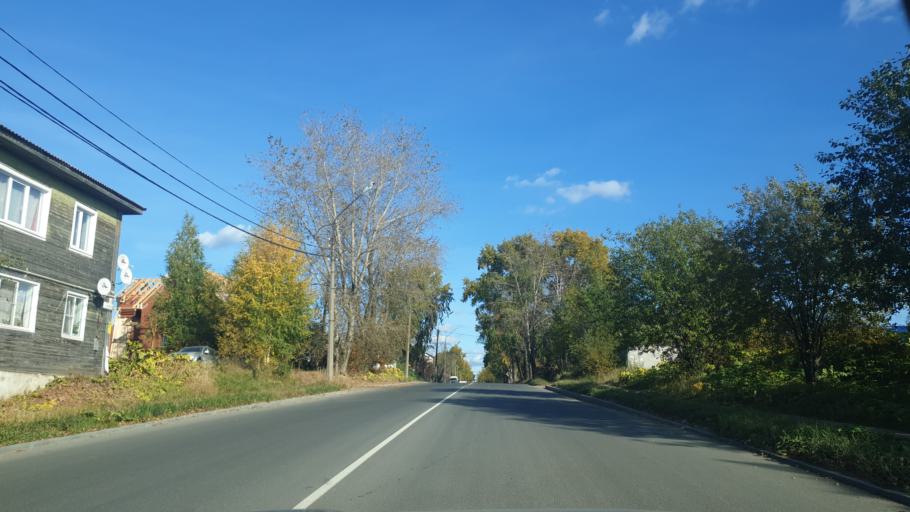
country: RU
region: Komi Republic
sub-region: Syktyvdinskiy Rayon
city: Syktyvkar
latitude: 61.6850
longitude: 50.7999
